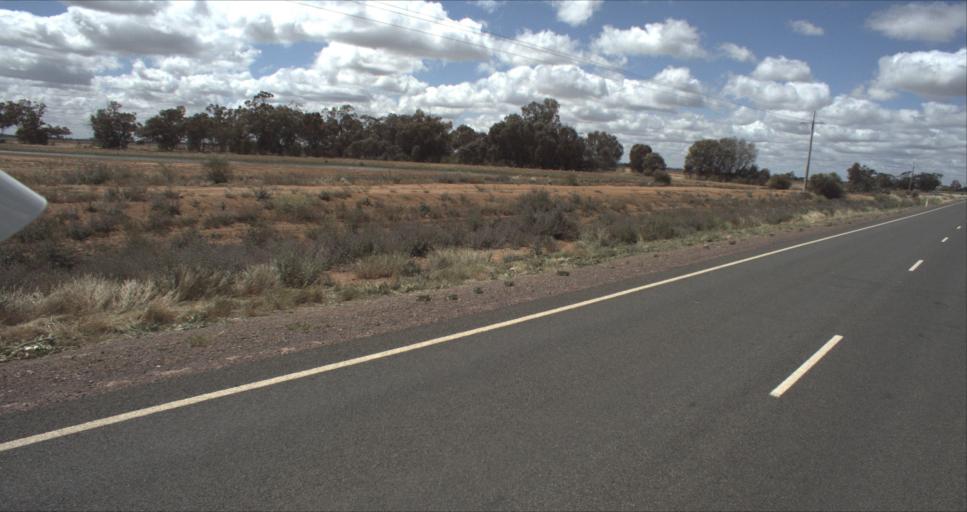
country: AU
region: New South Wales
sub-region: Murrumbidgee Shire
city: Darlington Point
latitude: -34.4804
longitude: 146.1538
